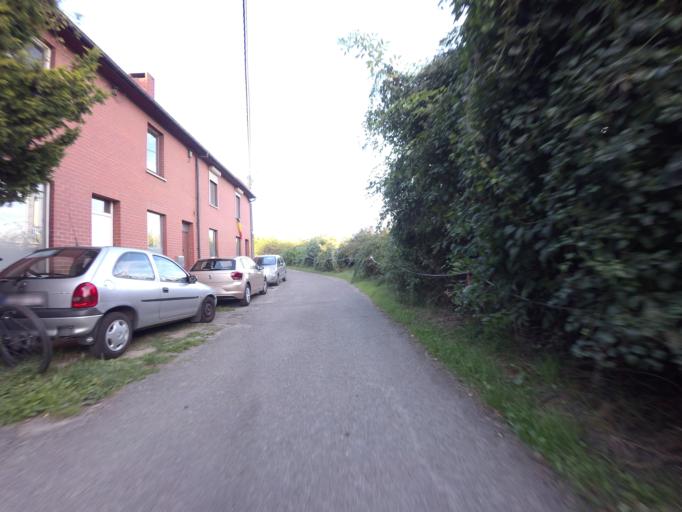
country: BE
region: Flanders
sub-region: Provincie Vlaams-Brabant
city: Leuven
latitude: 50.8995
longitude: 4.6969
